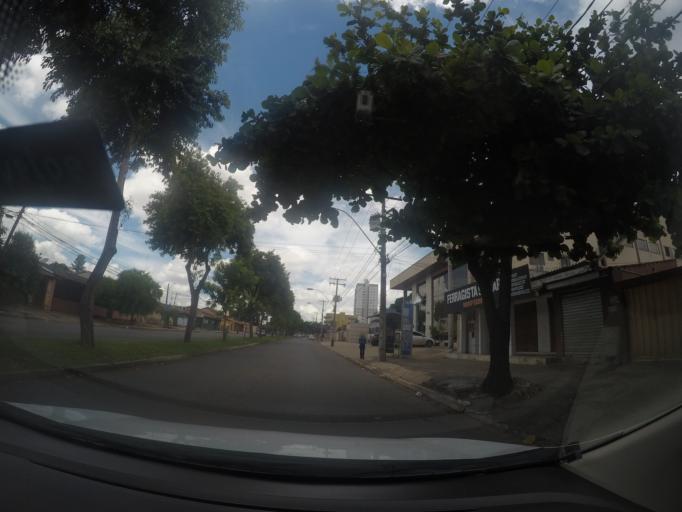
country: BR
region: Goias
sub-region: Goiania
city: Goiania
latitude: -16.6823
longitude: -49.3002
